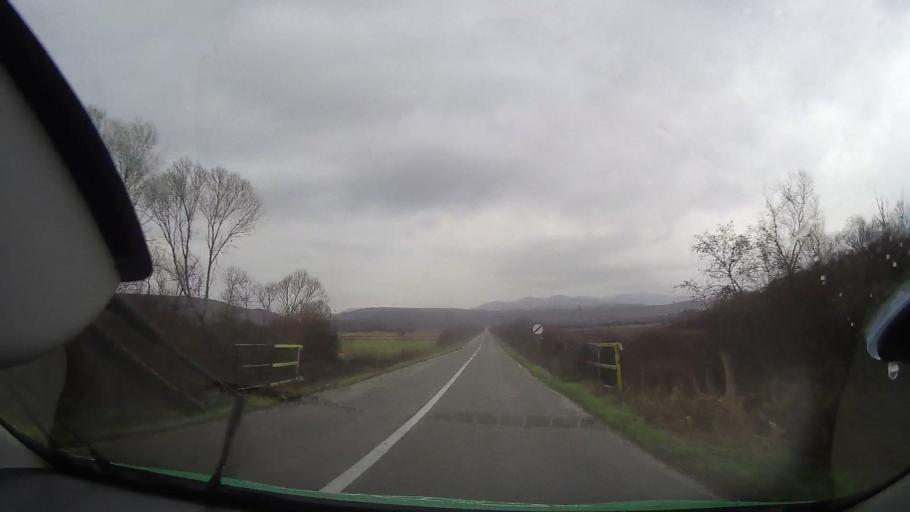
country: RO
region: Bihor
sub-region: Comuna Soimi
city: Soimi
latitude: 46.6947
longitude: 22.0952
